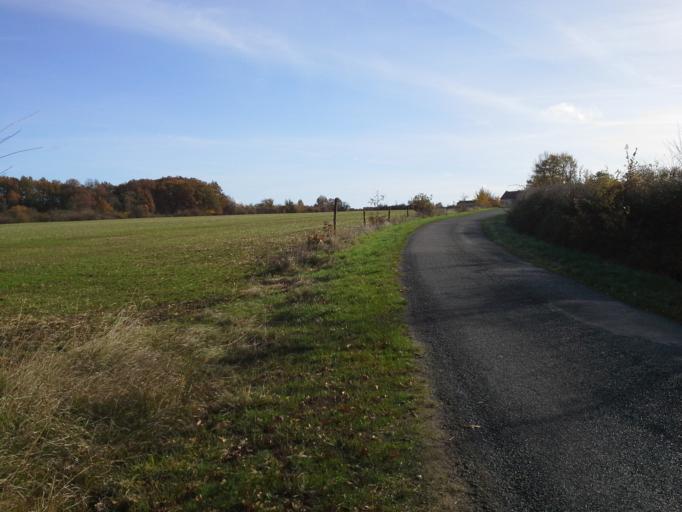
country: FR
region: Poitou-Charentes
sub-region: Departement de la Vienne
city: Pleumartin
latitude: 46.6393
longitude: 0.7654
